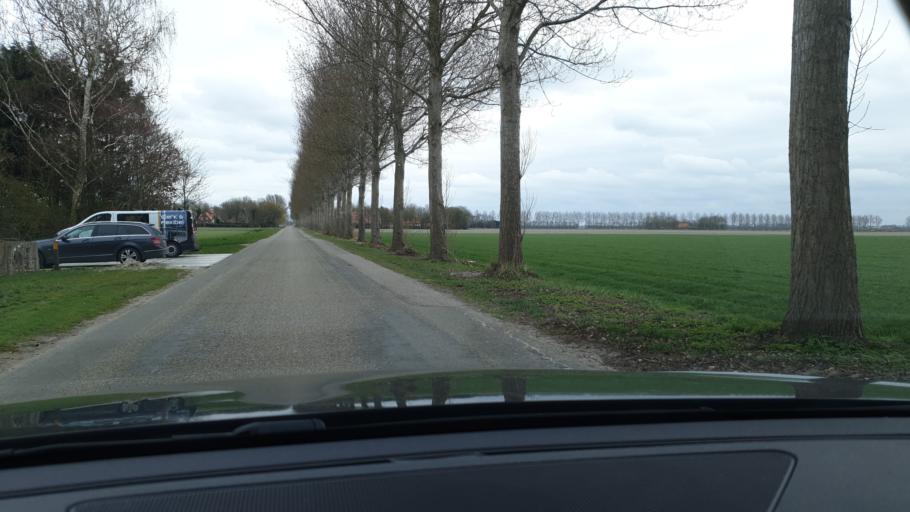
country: NL
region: Flevoland
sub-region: Gemeente Urk
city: Urk
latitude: 52.7392
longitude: 5.6331
